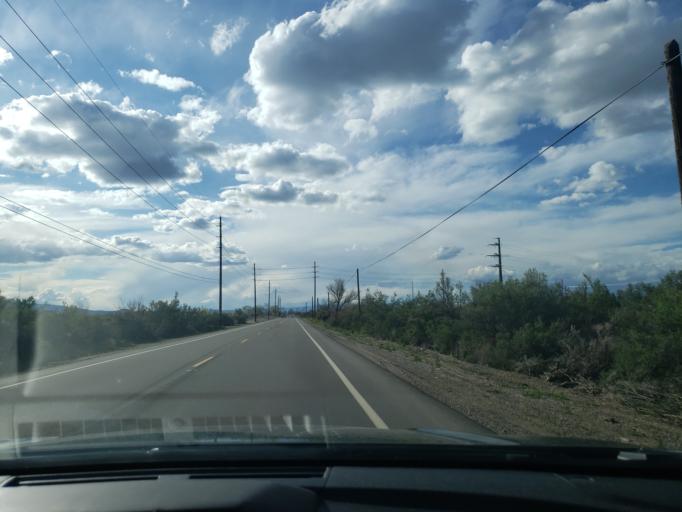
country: US
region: Colorado
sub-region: Mesa County
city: Redlands
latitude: 39.1135
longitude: -108.6530
